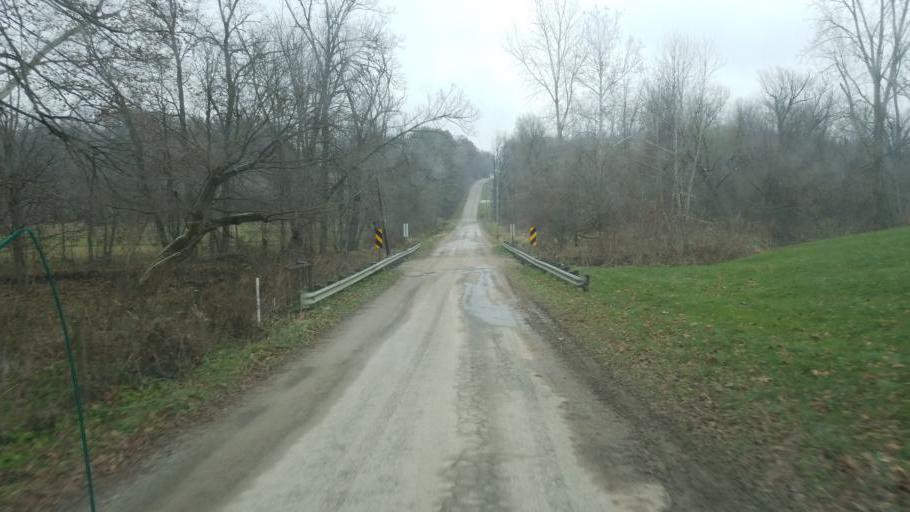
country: US
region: Ohio
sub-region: Huron County
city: New London
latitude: 40.9754
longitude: -82.3824
